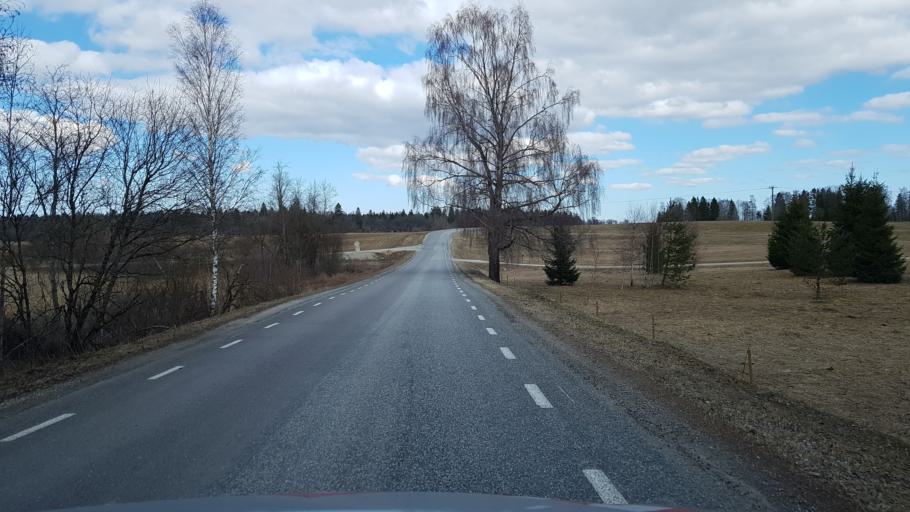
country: EE
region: Laeaene-Virumaa
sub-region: Kadrina vald
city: Kadrina
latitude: 59.2416
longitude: 26.1860
